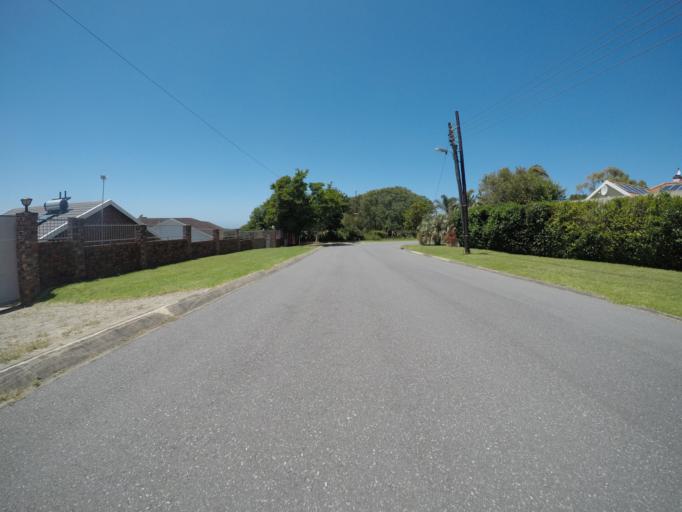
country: ZA
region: Eastern Cape
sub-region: Buffalo City Metropolitan Municipality
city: East London
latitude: -32.9655
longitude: 27.9549
